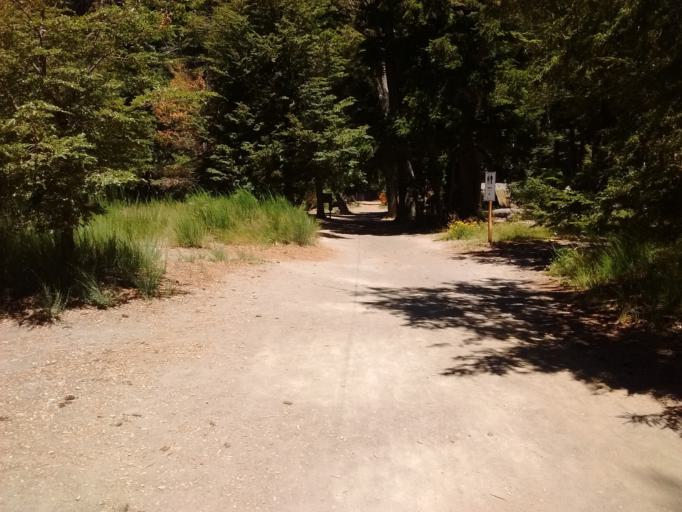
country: AR
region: Neuquen
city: Villa La Angostura
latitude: -40.7835
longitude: -71.6601
